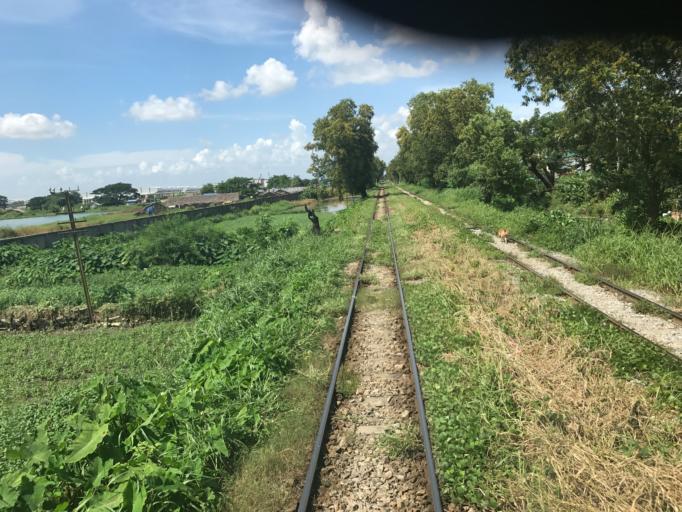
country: MM
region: Yangon
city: Yangon
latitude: 16.9247
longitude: 96.0935
